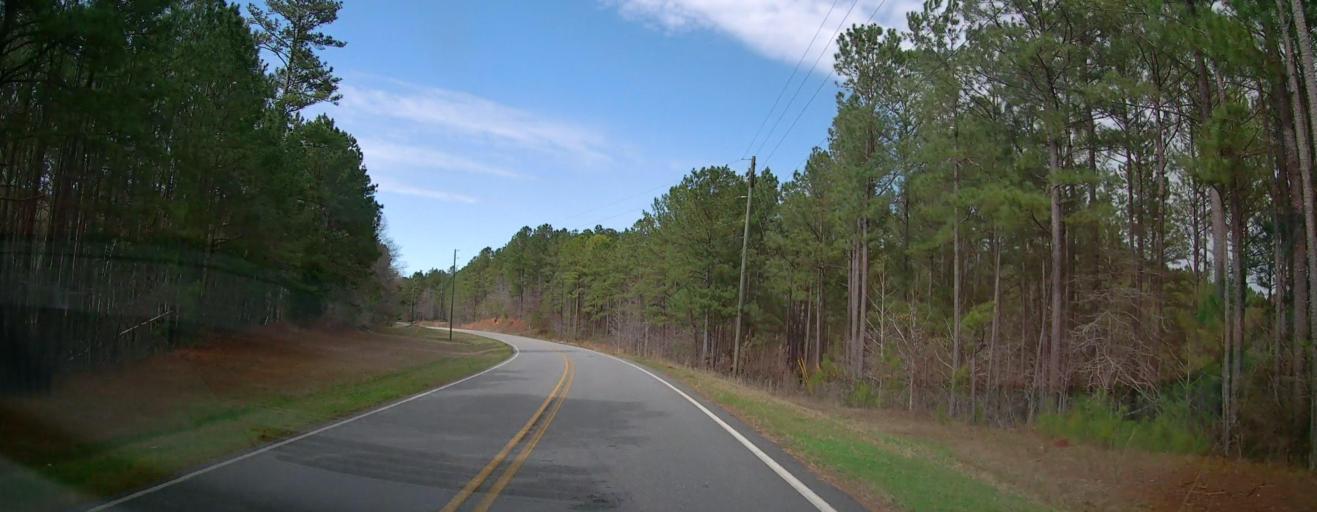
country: US
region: Georgia
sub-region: Jones County
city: Gray
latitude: 33.0586
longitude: -83.7240
